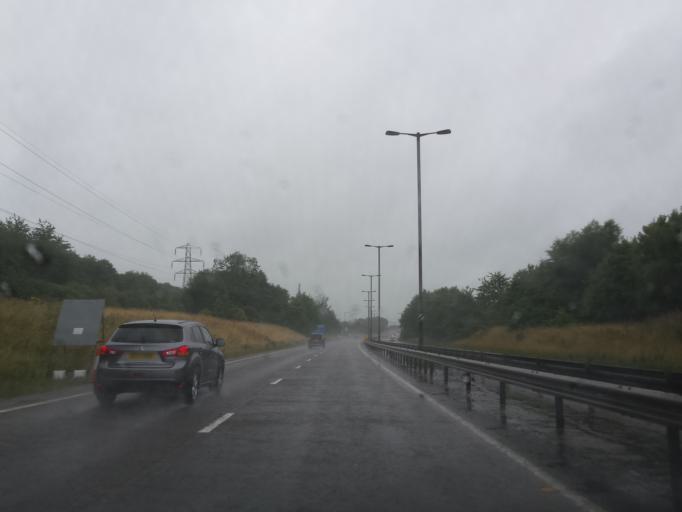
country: GB
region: England
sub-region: Warwickshire
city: Ryton on Dunsmore
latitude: 52.3925
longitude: -1.4350
